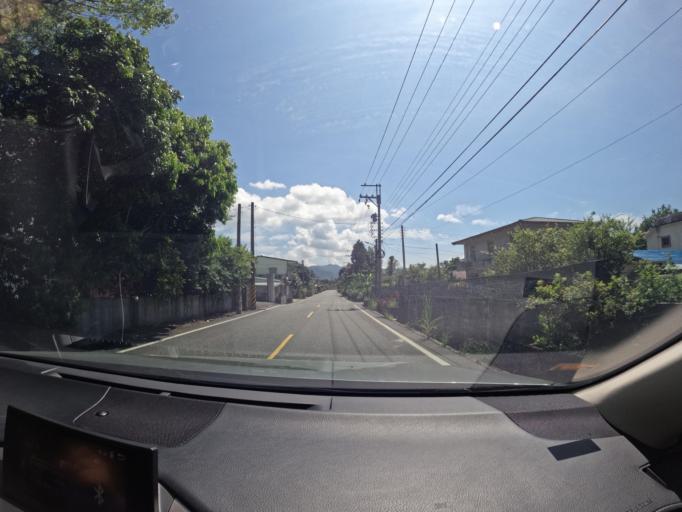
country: TW
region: Taiwan
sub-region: Hualien
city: Hualian
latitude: 23.5838
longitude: 121.3642
